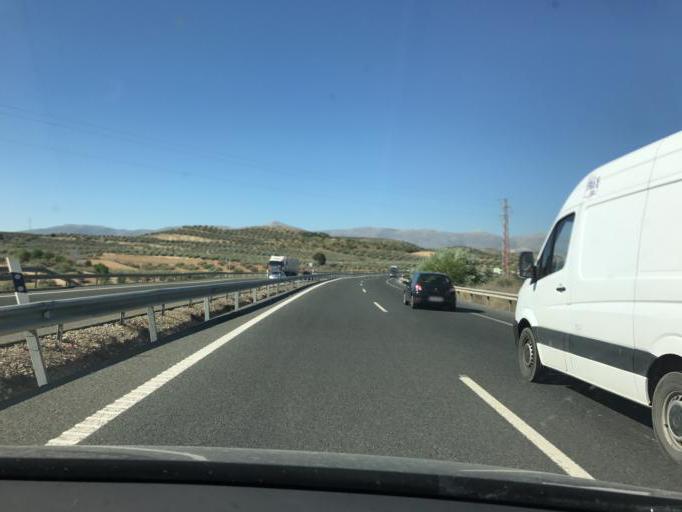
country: ES
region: Andalusia
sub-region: Provincia de Granada
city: Huetor-Tajar
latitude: 37.1845
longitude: -4.0337
